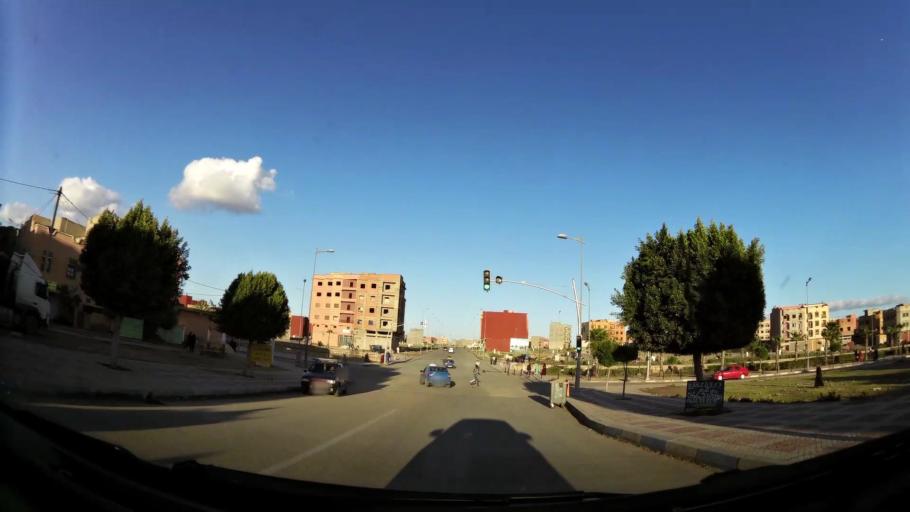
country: MA
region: Marrakech-Tensift-Al Haouz
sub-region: Kelaa-Des-Sraghna
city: Sidi Abdallah
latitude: 32.2395
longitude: -7.9502
